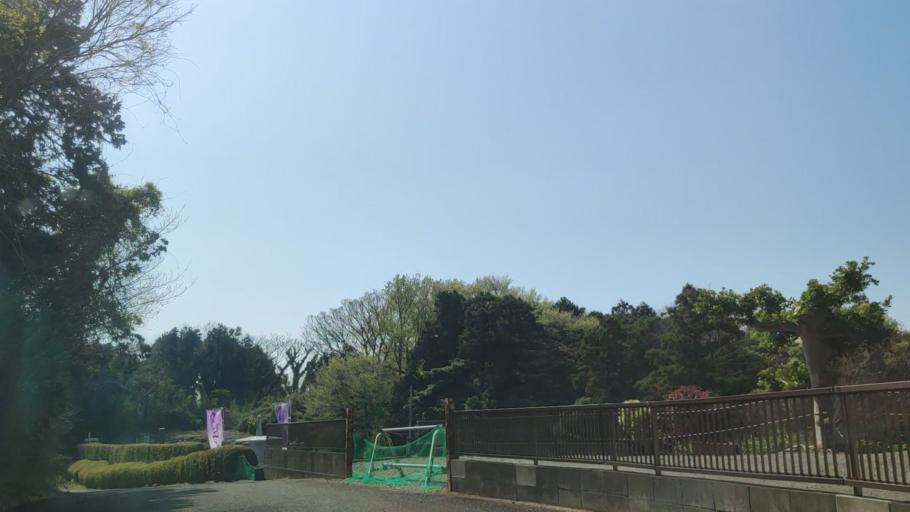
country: JP
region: Kanagawa
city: Ninomiya
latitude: 35.3251
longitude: 139.2698
